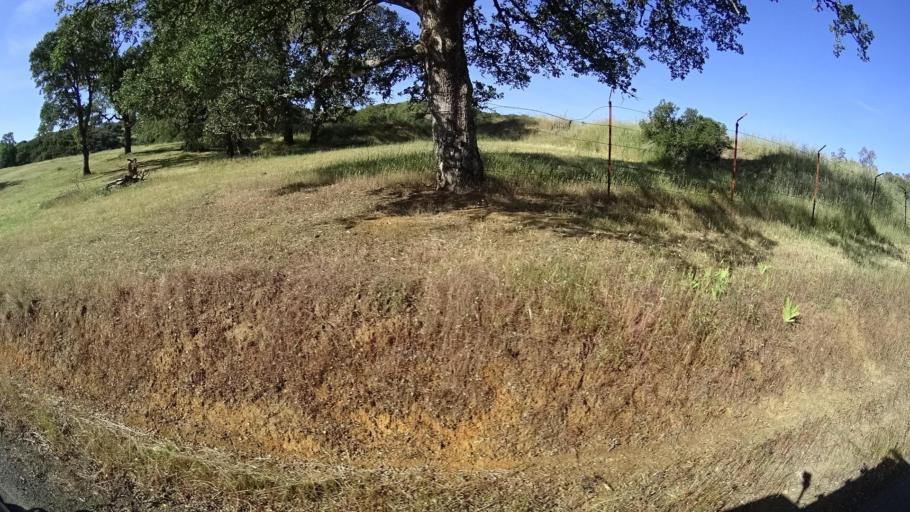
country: US
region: California
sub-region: Lake County
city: Lakeport
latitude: 39.0417
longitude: -122.9460
